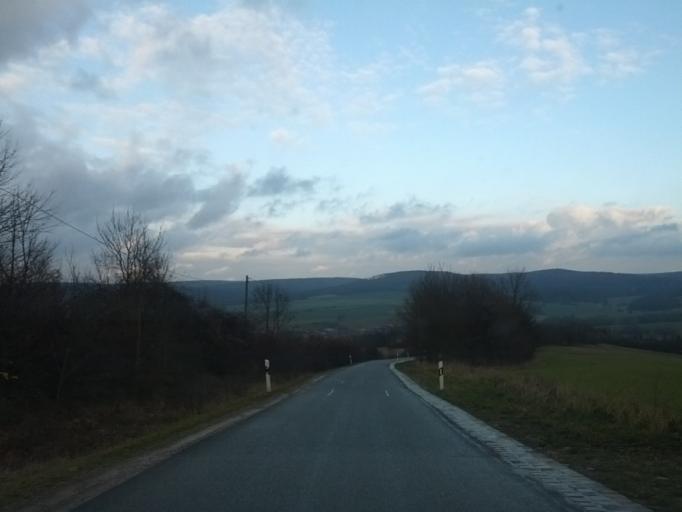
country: DE
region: Thuringia
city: Bischofroda
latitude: 51.0450
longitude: 10.3541
